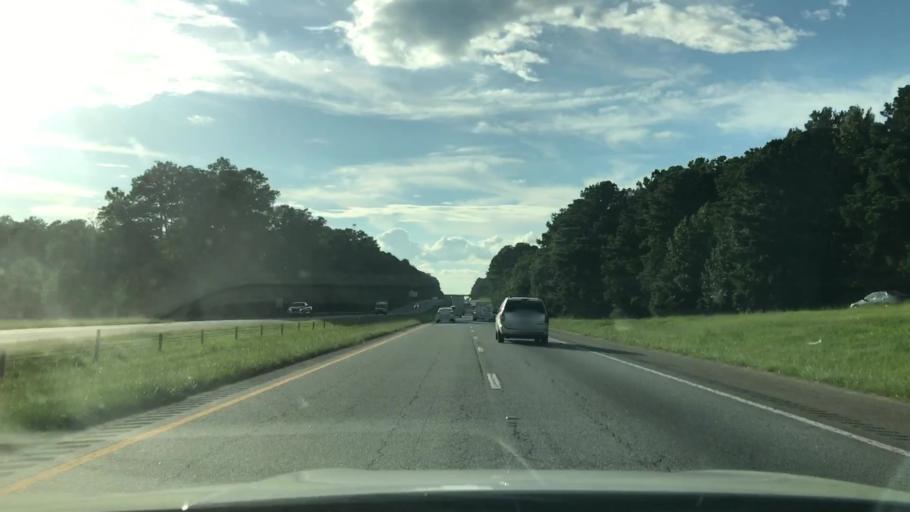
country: US
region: South Carolina
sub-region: Newberry County
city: Newberry
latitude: 34.3126
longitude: -81.5753
